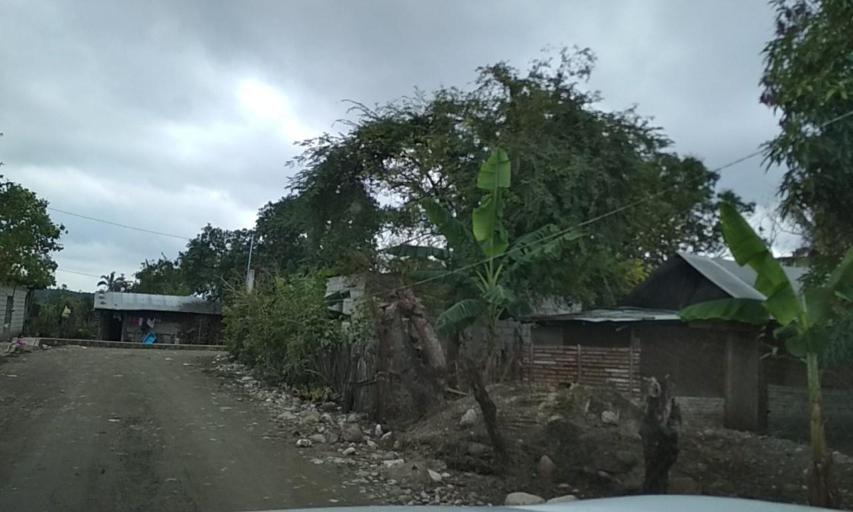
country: MX
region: Veracruz
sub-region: Papantla
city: El Chote
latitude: 20.3651
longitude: -97.4284
